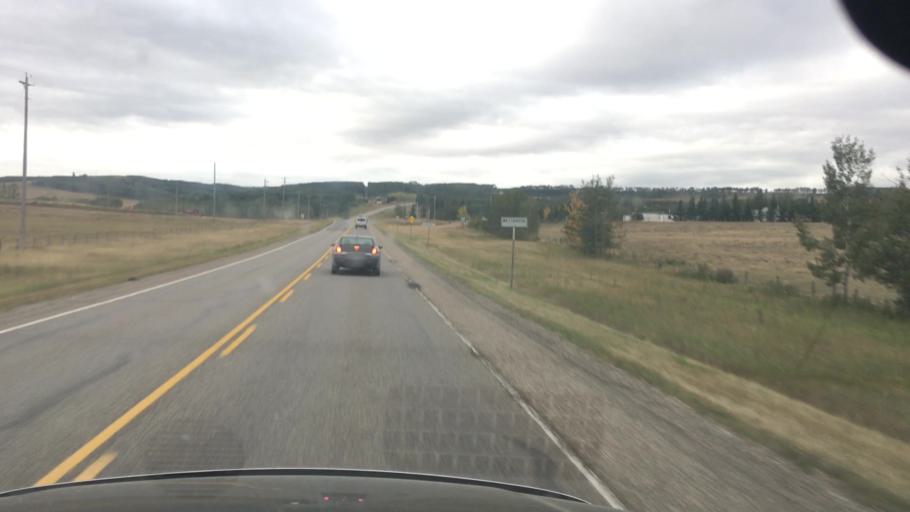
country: CA
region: Alberta
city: Cochrane
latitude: 51.3772
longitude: -114.4703
